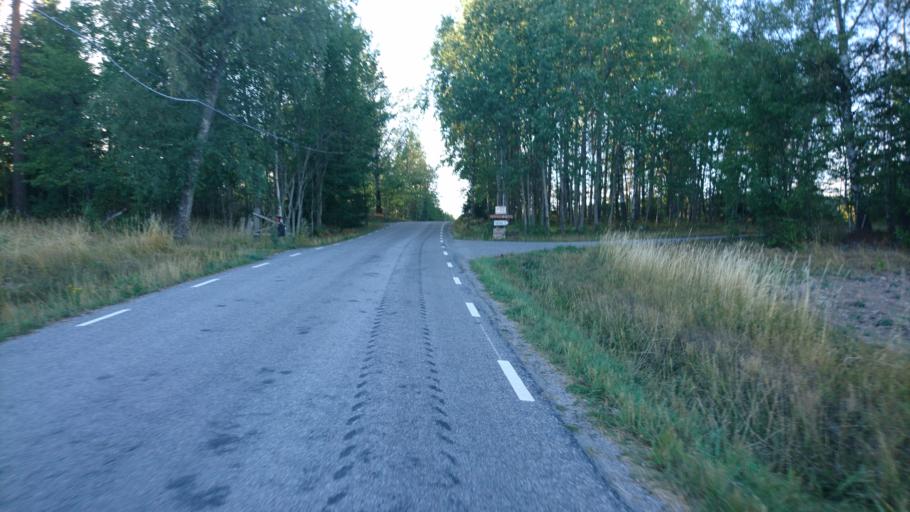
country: SE
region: Soedermanland
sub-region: Strangnas Kommun
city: Stallarholmen
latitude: 59.3952
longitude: 17.2673
